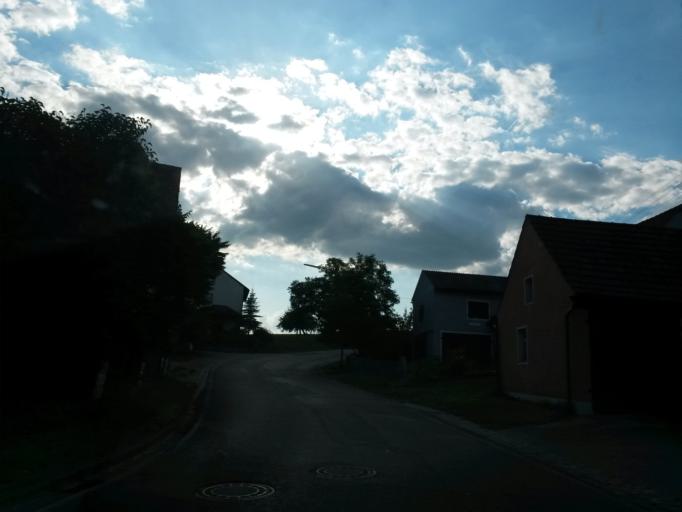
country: DE
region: Bavaria
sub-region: Regierungsbezirk Mittelfranken
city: Munchsteinach
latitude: 49.6661
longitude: 10.5790
